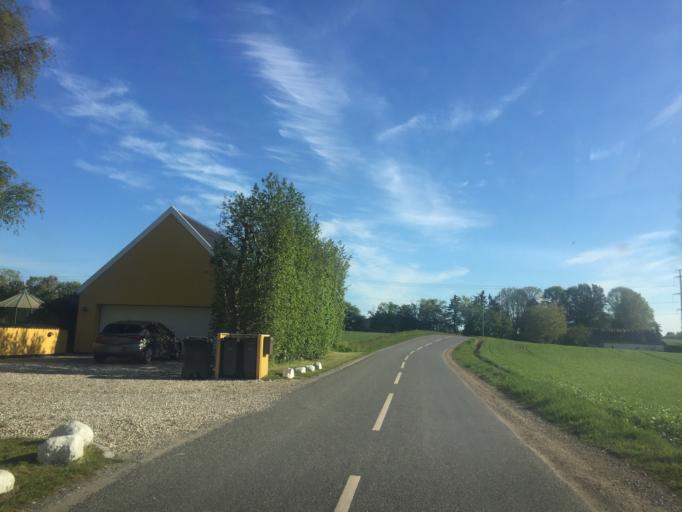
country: DK
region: Capital Region
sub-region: Egedal Kommune
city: Vekso
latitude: 55.7275
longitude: 12.2627
